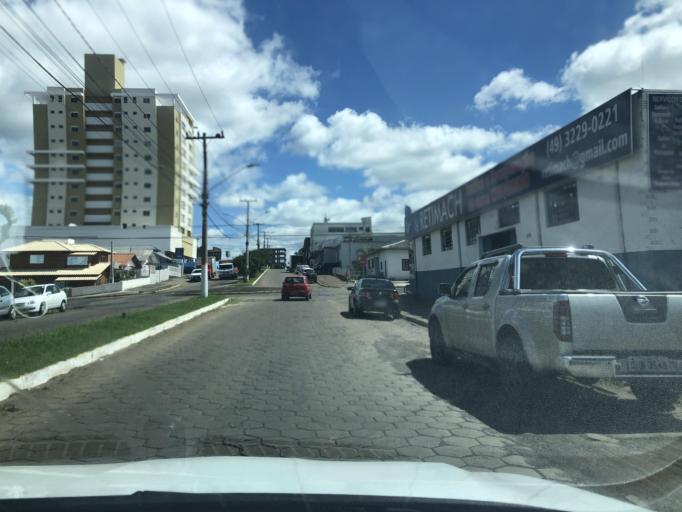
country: BR
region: Santa Catarina
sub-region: Lages
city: Lages
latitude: -27.8141
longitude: -50.3136
